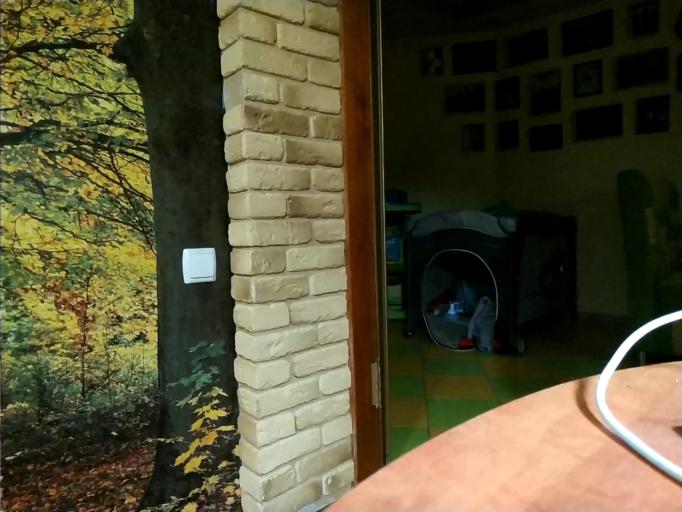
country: RU
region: Moskovskaya
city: Istra
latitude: 56.0764
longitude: 36.7713
